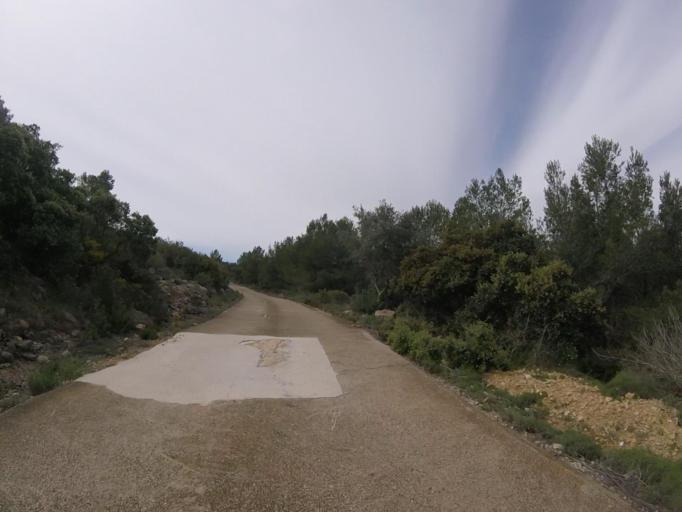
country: ES
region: Valencia
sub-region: Provincia de Castello
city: Cabanes
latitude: 40.1912
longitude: 0.0788
